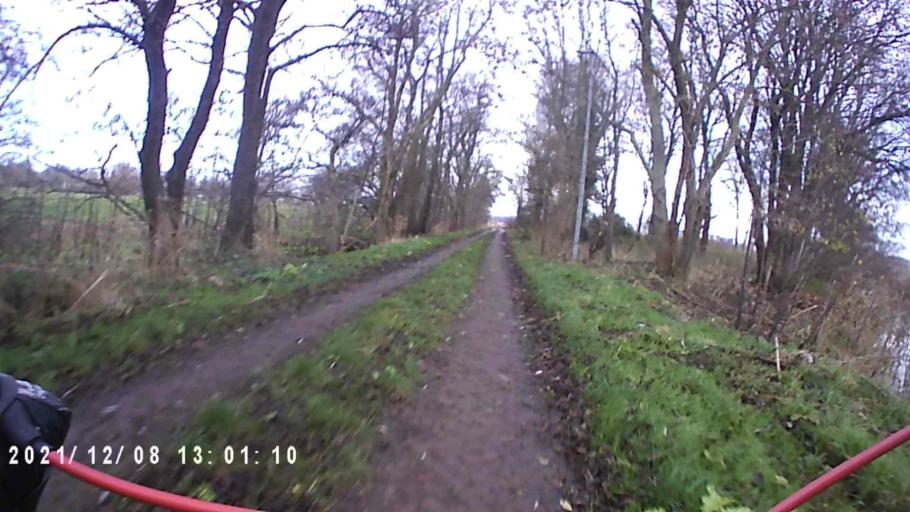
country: NL
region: Groningen
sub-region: Gemeente Haren
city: Haren
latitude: 53.2024
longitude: 6.6259
